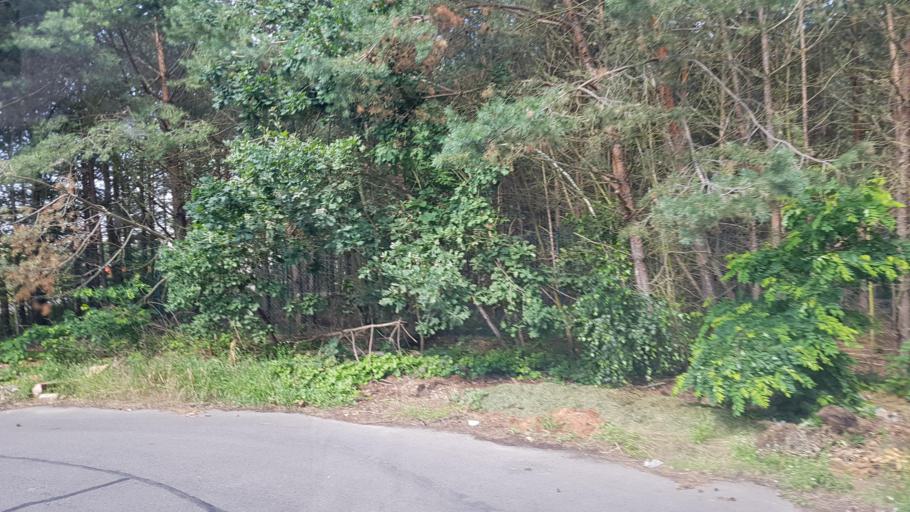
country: DE
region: Brandenburg
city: Grossraschen
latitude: 51.5967
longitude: 14.0194
